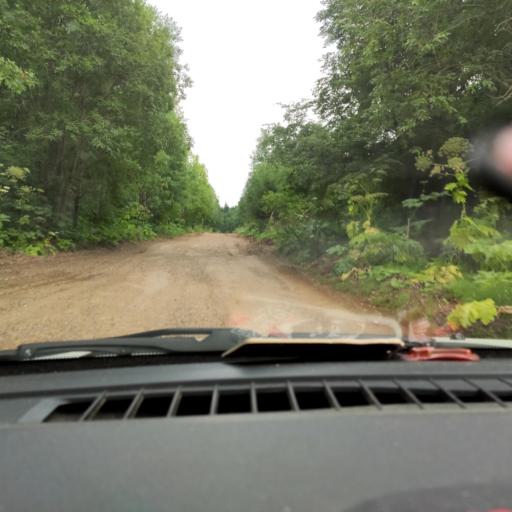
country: RU
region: Perm
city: Kultayevo
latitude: 57.8173
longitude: 56.0004
